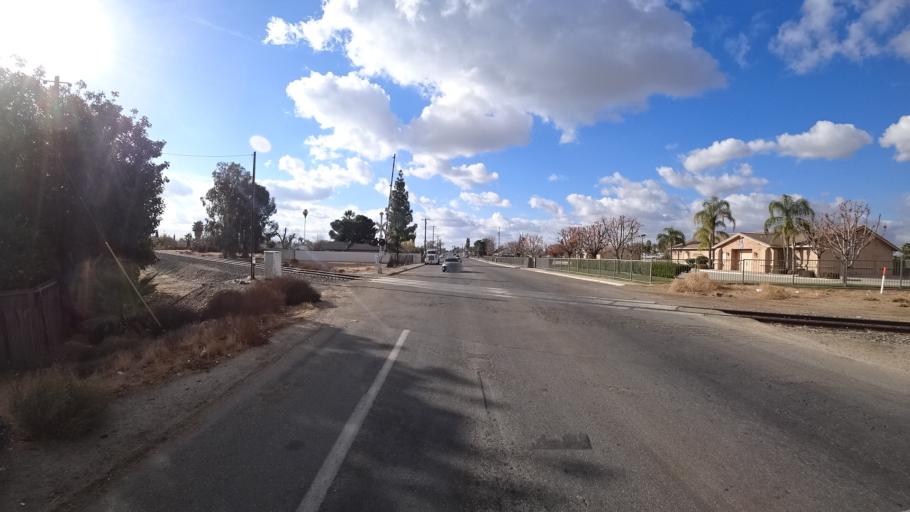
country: US
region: California
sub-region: Kern County
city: Bakersfield
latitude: 35.3322
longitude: -119.0102
